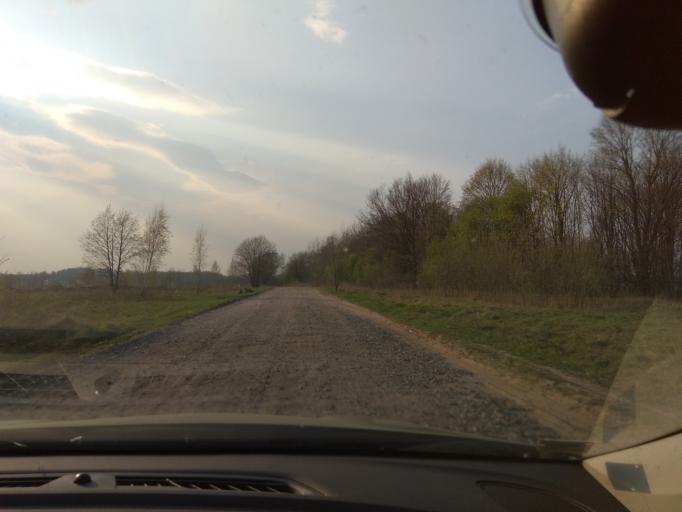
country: LT
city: Baltoji Voke
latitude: 54.5934
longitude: 25.1686
